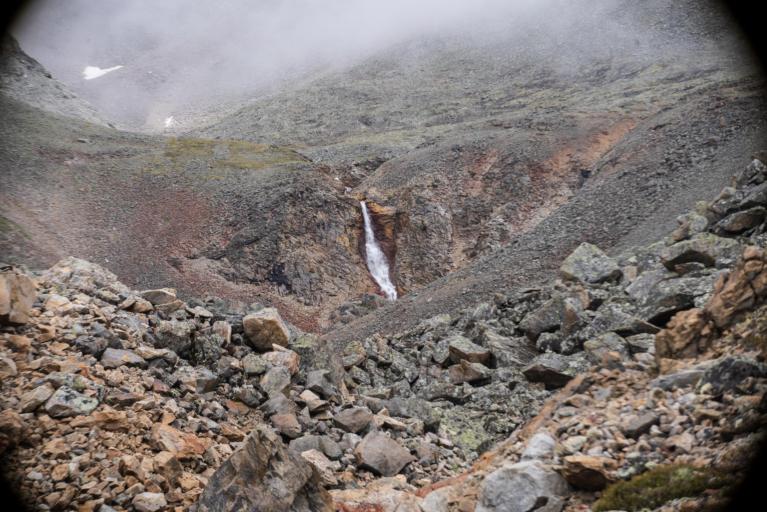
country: RU
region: Transbaikal Territory
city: Chara
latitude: 56.8644
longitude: 117.6417
